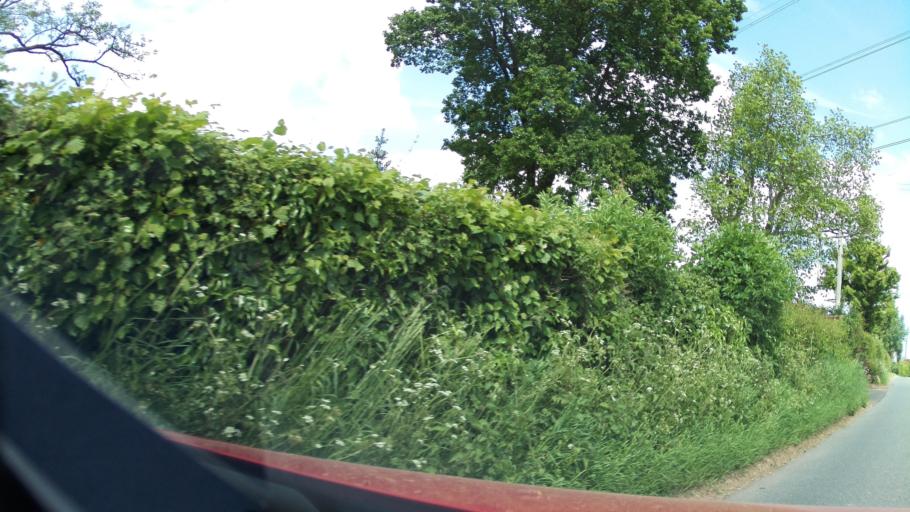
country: GB
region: England
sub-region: Herefordshire
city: Sellack
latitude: 51.9224
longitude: -2.6594
